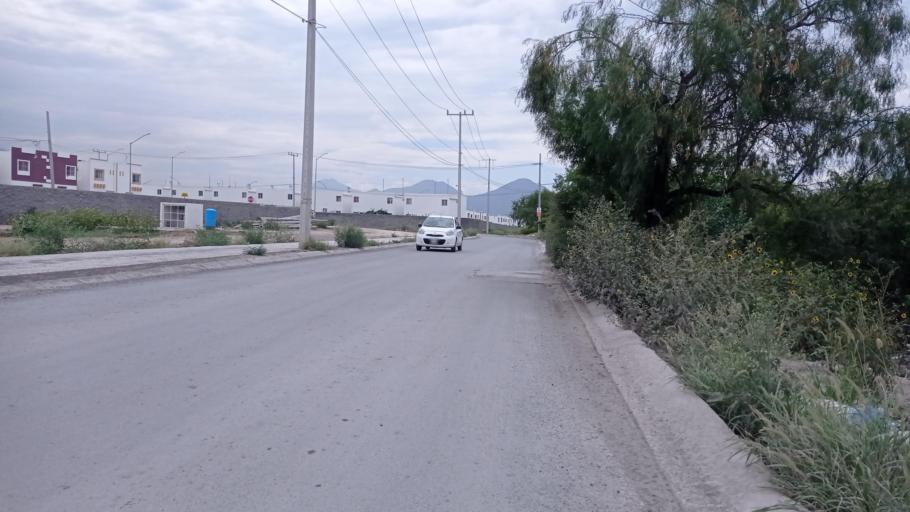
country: MX
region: Nuevo Leon
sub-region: Salinas Victoria
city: Simeprodeso (Colectivo Nuevo)
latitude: 25.8766
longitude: -100.3146
